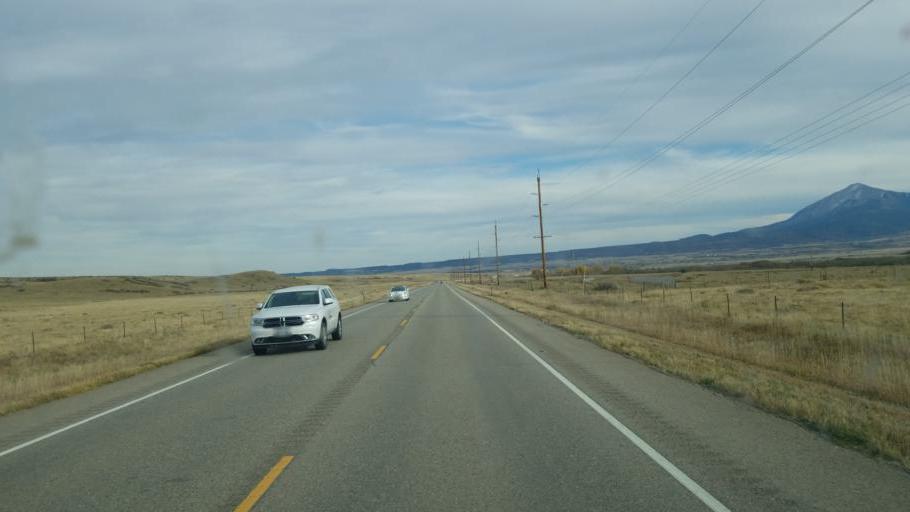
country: US
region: Colorado
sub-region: Huerfano County
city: Walsenburg
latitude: 37.5448
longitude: -105.0823
